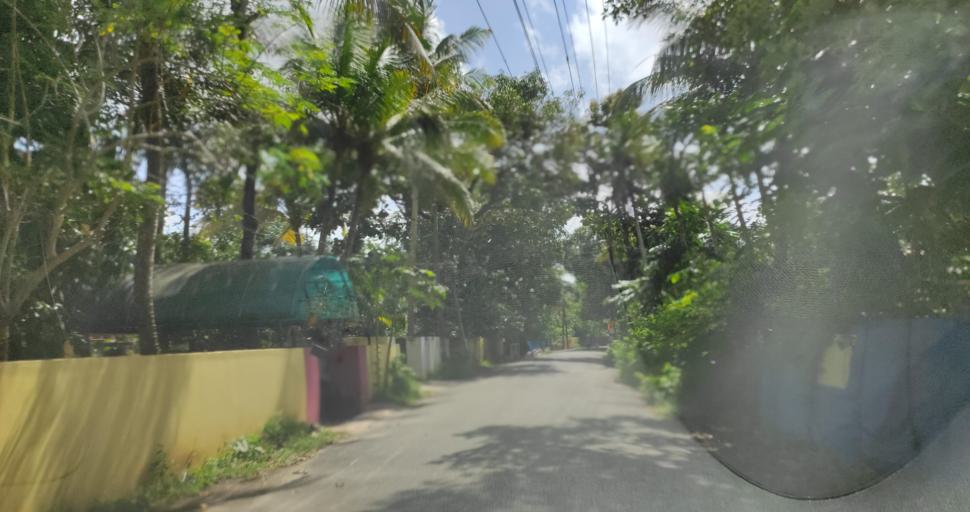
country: IN
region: Kerala
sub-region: Alappuzha
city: Shertallai
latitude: 9.6638
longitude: 76.3798
